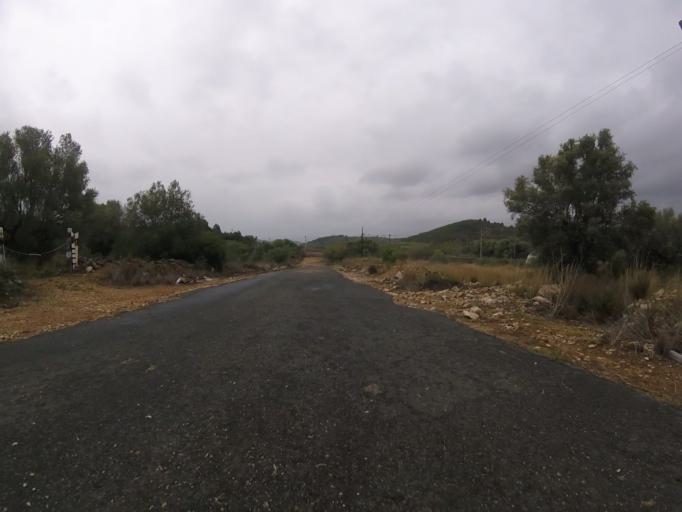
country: ES
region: Valencia
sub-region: Provincia de Castello
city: Alcala de Xivert
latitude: 40.2778
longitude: 0.2276
